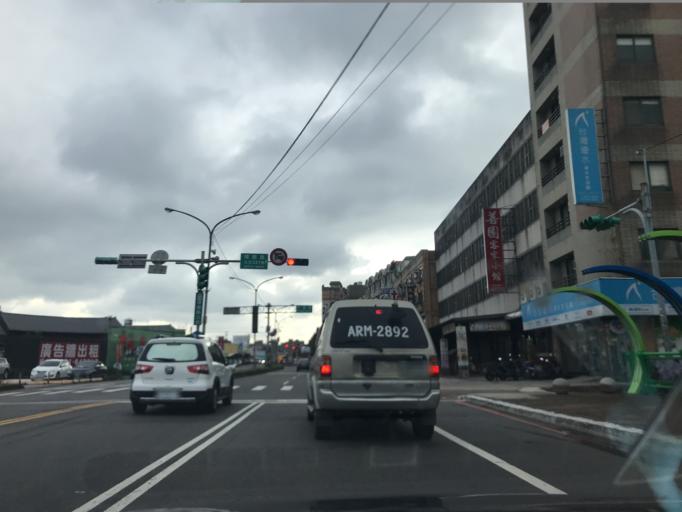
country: TW
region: Taiwan
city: Daxi
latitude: 24.9417
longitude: 121.2250
